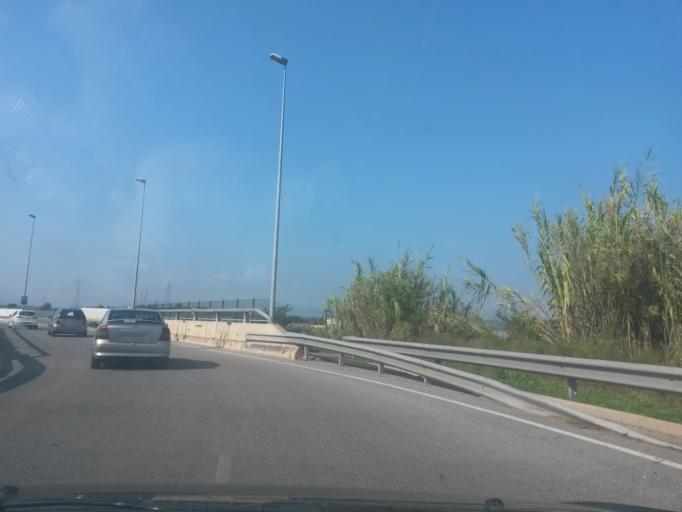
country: ES
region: Catalonia
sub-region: Provincia de Girona
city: Fornells de la Selva
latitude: 41.9429
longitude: 2.8058
